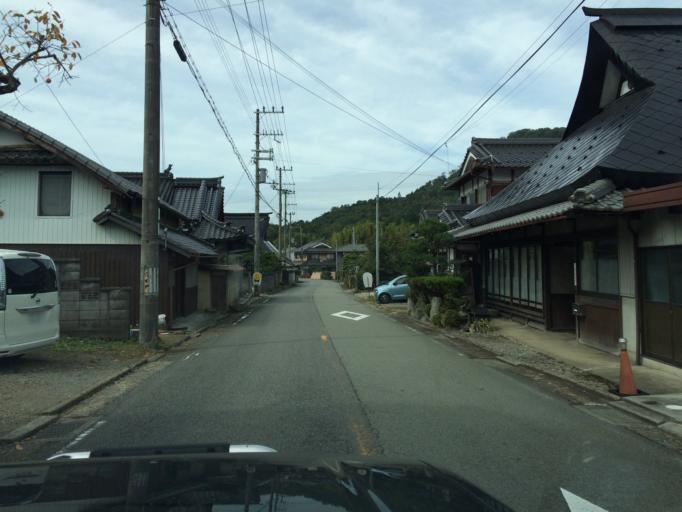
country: JP
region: Hyogo
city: Sasayama
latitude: 35.0697
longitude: 135.2933
